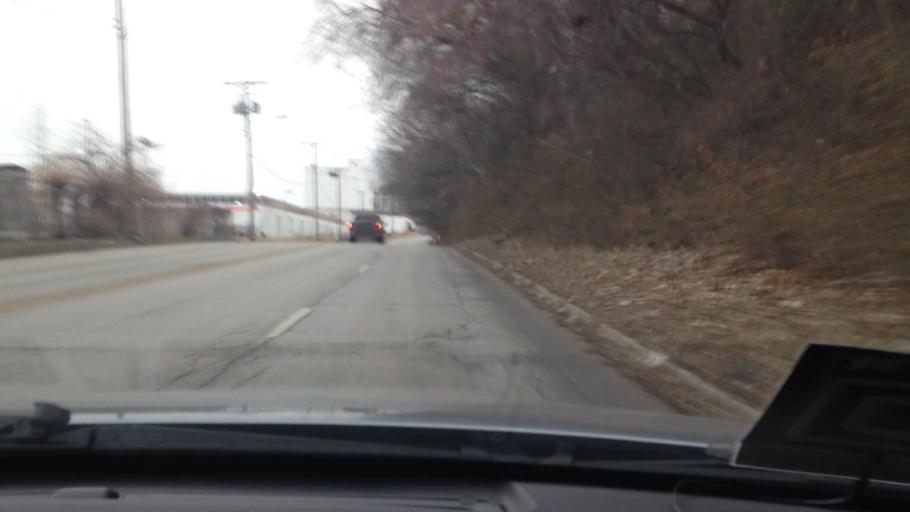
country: US
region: Missouri
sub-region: Clay County
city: North Kansas City
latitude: 39.1185
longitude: -94.5079
